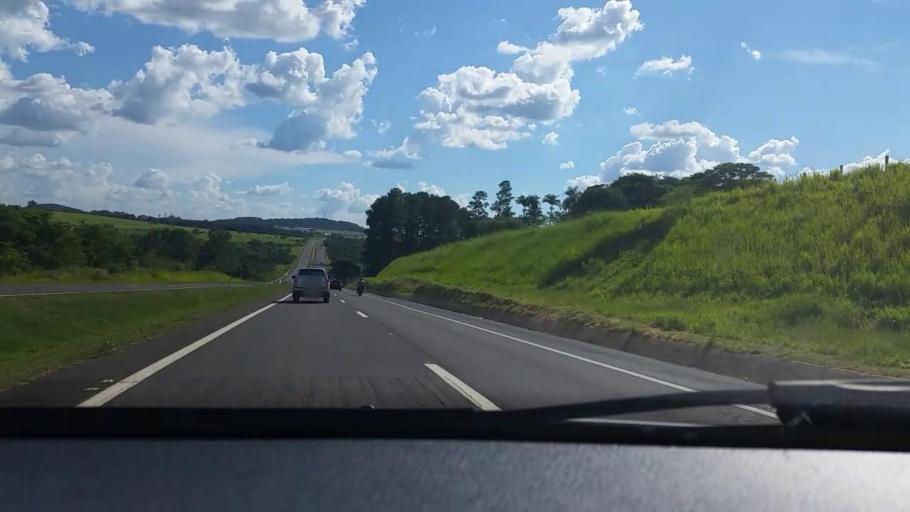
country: BR
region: Sao Paulo
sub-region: Bauru
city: Bauru
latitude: -22.4033
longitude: -49.0936
